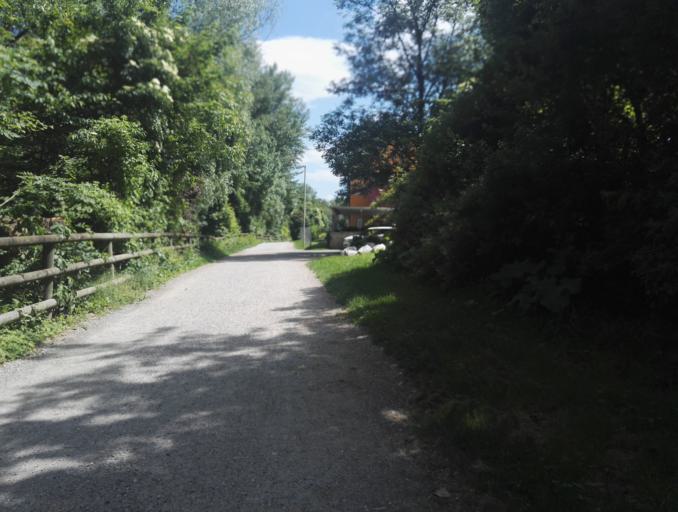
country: AT
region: Styria
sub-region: Graz Stadt
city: Goesting
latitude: 47.0907
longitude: 15.4209
